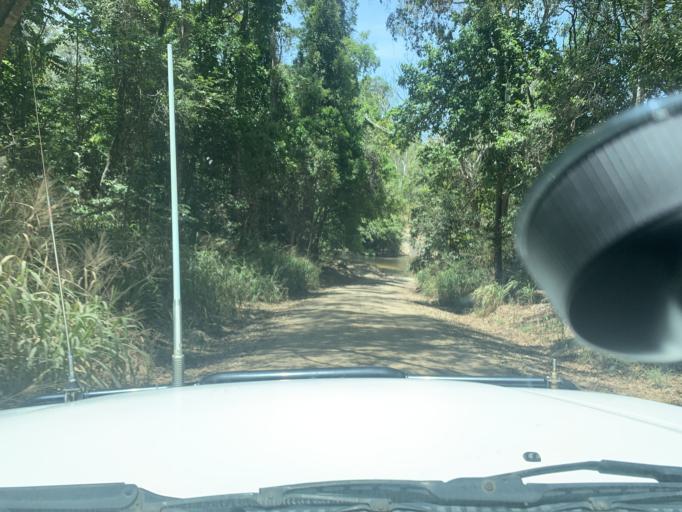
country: AU
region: Queensland
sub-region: Tablelands
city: Kuranda
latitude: -16.9228
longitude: 145.5877
